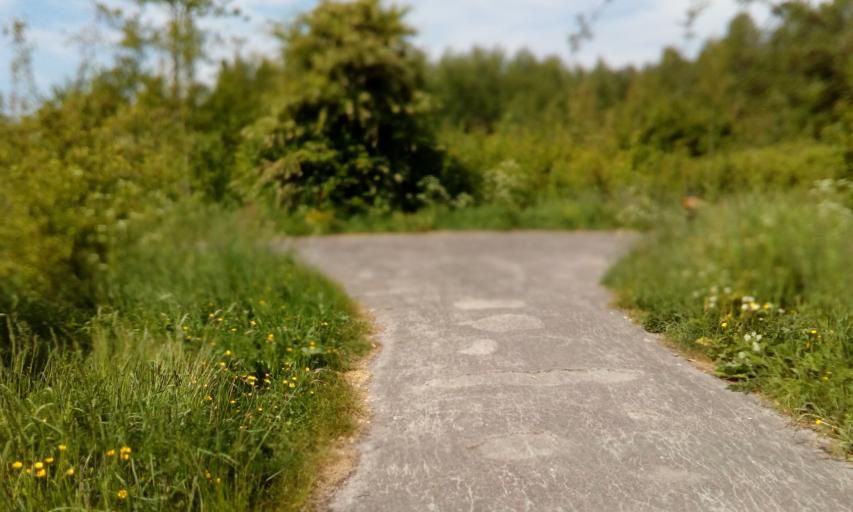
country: NL
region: South Holland
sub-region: Gemeente Pijnacker-Nootdorp
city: Pijnacker
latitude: 52.0460
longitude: 4.4426
